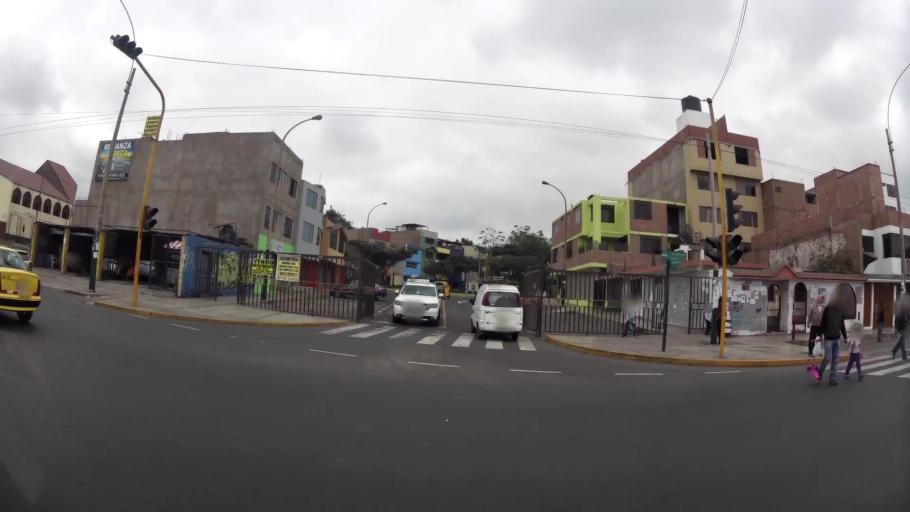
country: PE
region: Lima
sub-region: Lima
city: Surco
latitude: -12.1586
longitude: -76.9887
